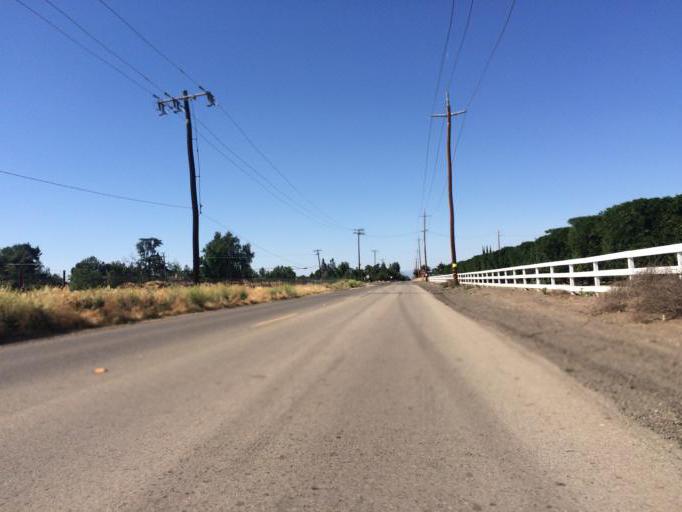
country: US
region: California
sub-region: Fresno County
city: Sanger
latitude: 36.7487
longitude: -119.6101
